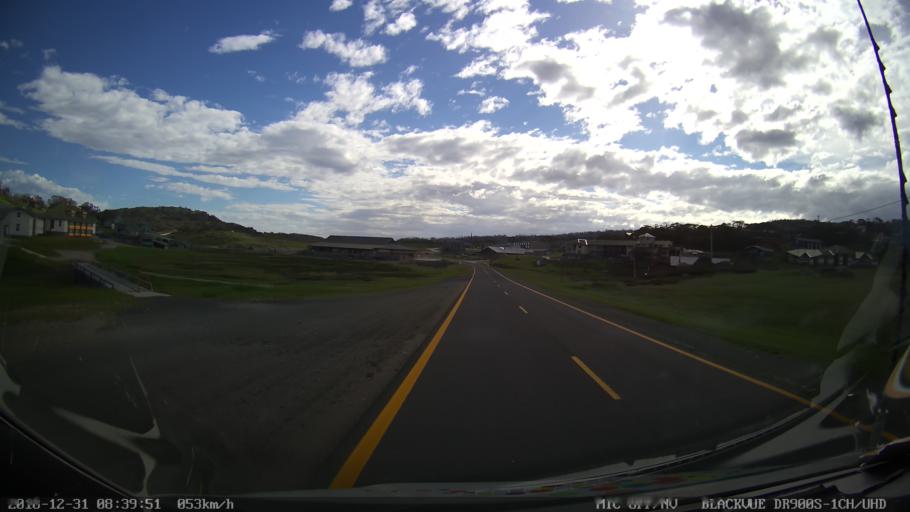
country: AU
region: New South Wales
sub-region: Snowy River
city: Jindabyne
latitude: -36.4068
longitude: 148.4092
